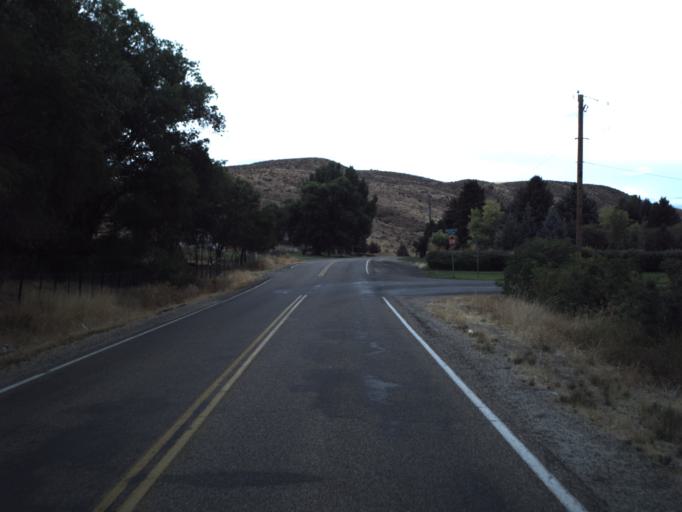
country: US
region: Utah
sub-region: Morgan County
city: Morgan
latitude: 41.0087
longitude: -111.6765
